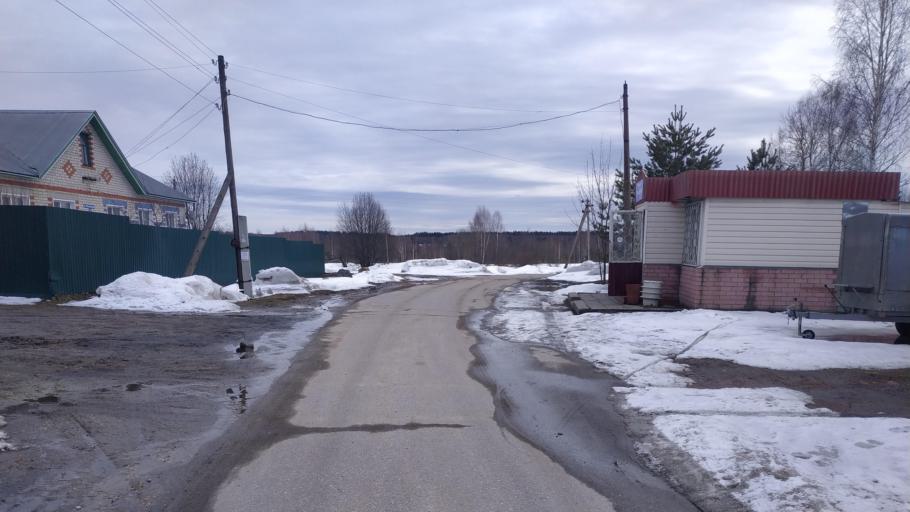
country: RU
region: Nizjnij Novgorod
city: Semenov
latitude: 56.7763
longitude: 44.2883
